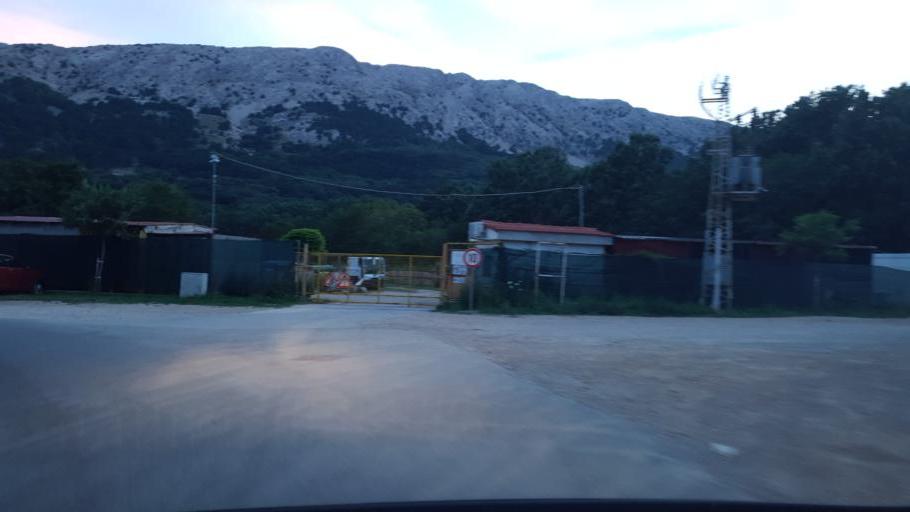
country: HR
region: Primorsko-Goranska
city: Punat
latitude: 44.9690
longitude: 14.7431
